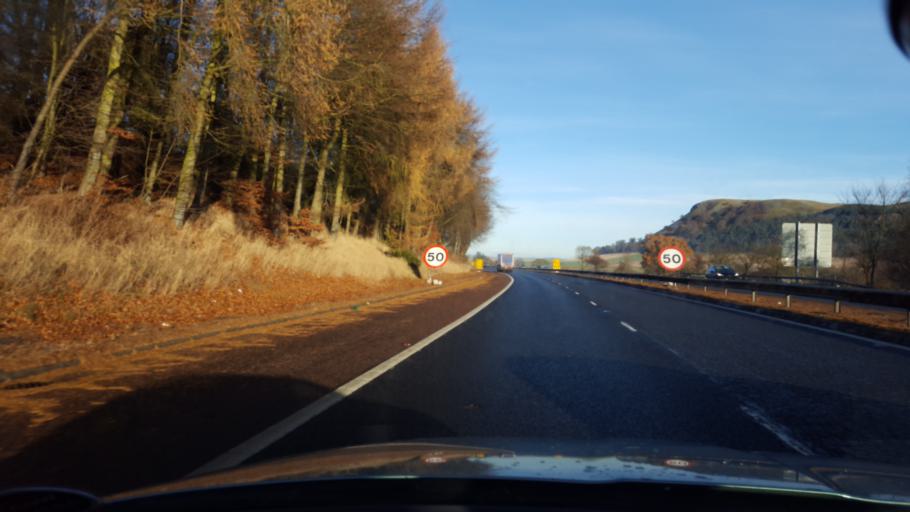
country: GB
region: Scotland
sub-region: Fife
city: Kelty
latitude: 56.1465
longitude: -3.3931
